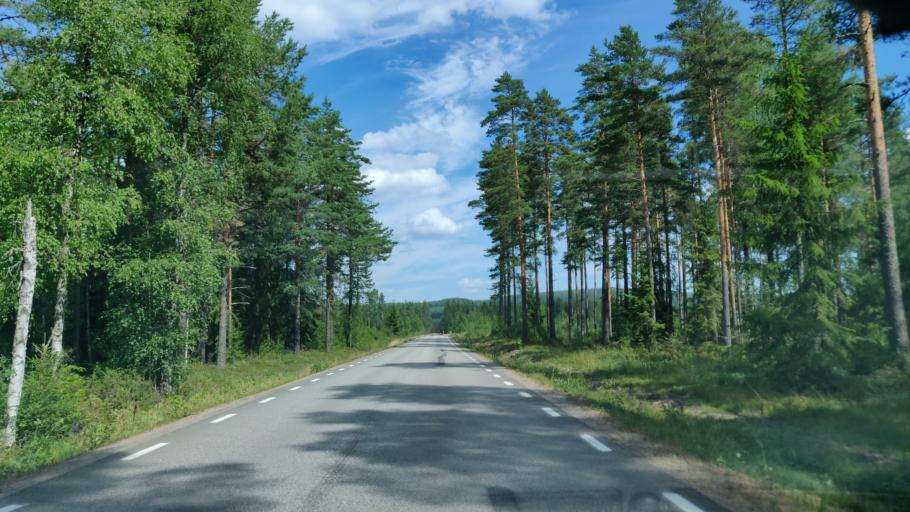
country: SE
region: Vaermland
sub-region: Hagfors Kommun
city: Ekshaerad
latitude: 60.0780
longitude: 13.4964
